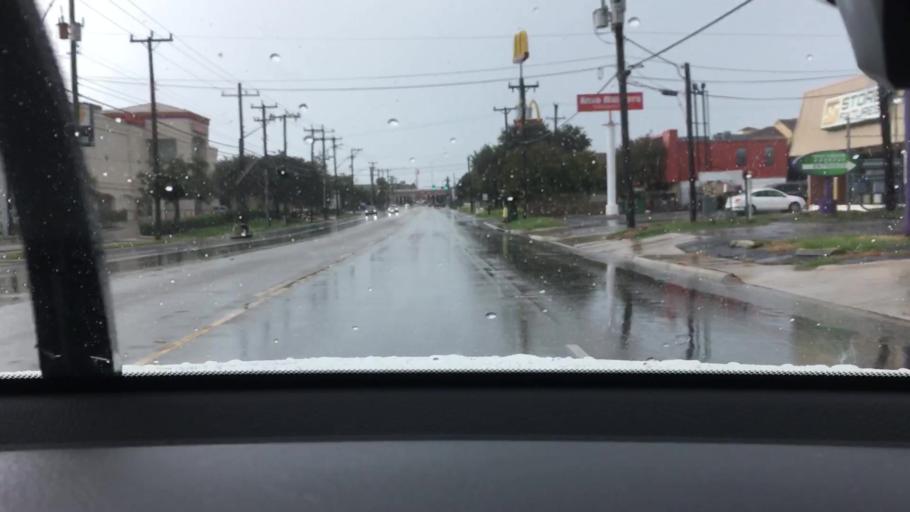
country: US
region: Texas
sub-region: Bexar County
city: Alamo Heights
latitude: 29.5205
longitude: -98.4610
